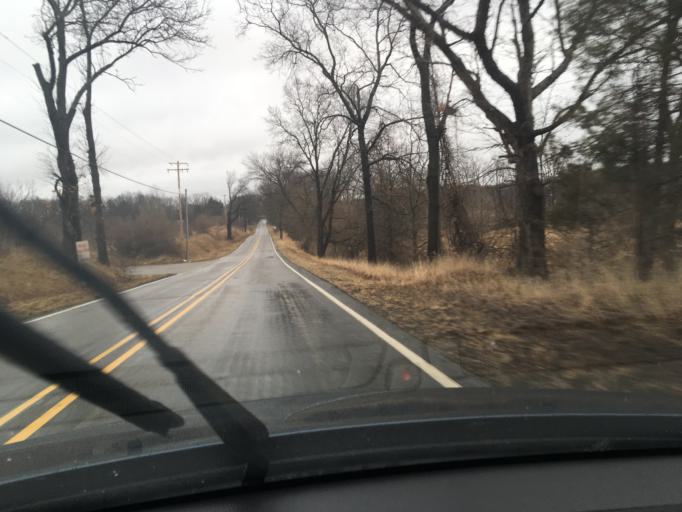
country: US
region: Michigan
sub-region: Jackson County
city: Grass Lake
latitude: 42.3412
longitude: -84.1469
